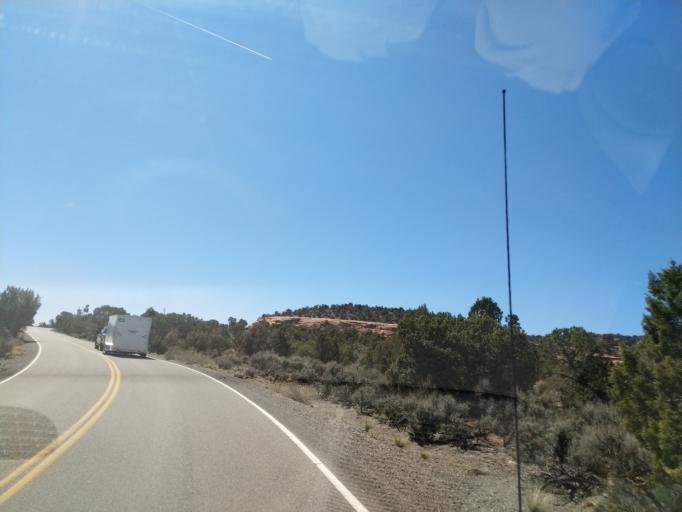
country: US
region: Colorado
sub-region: Mesa County
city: Redlands
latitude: 39.0236
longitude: -108.6601
